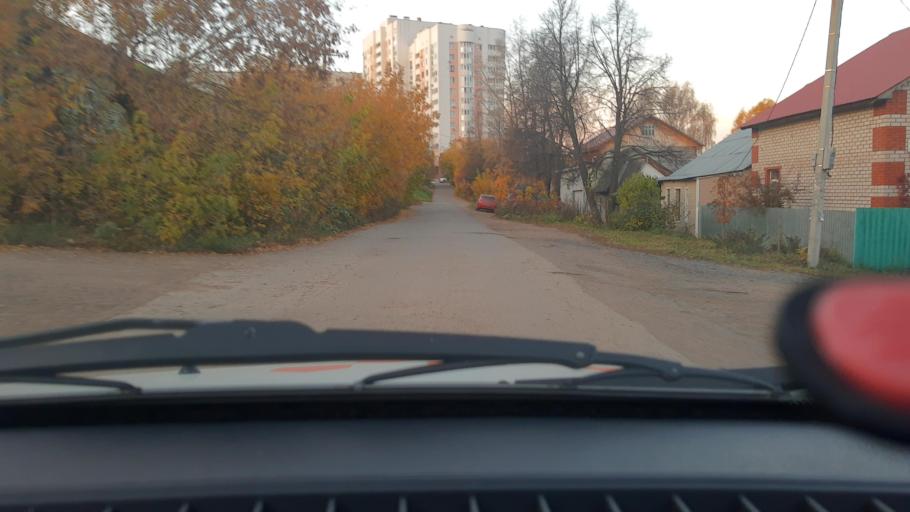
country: RU
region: Bashkortostan
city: Ufa
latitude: 54.7063
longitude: 55.9807
